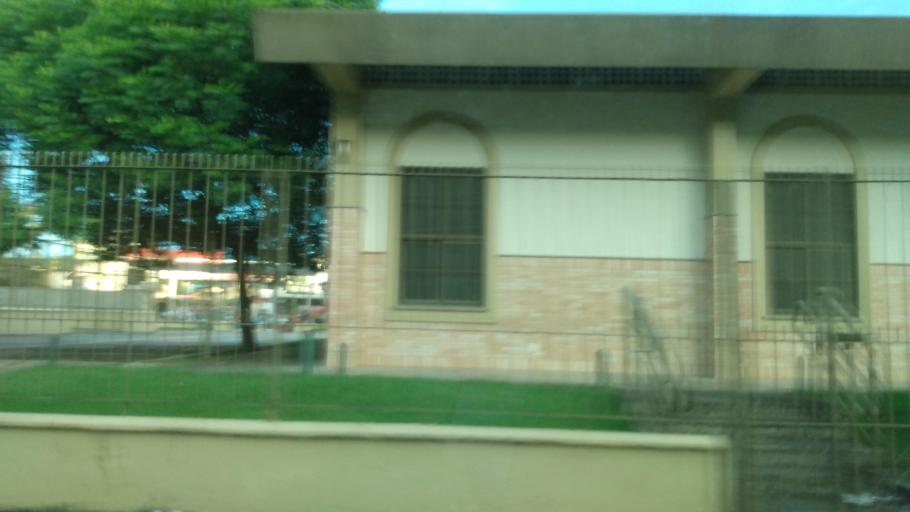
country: BR
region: Pernambuco
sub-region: Palmares
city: Palmares
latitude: -8.6830
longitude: -35.5879
